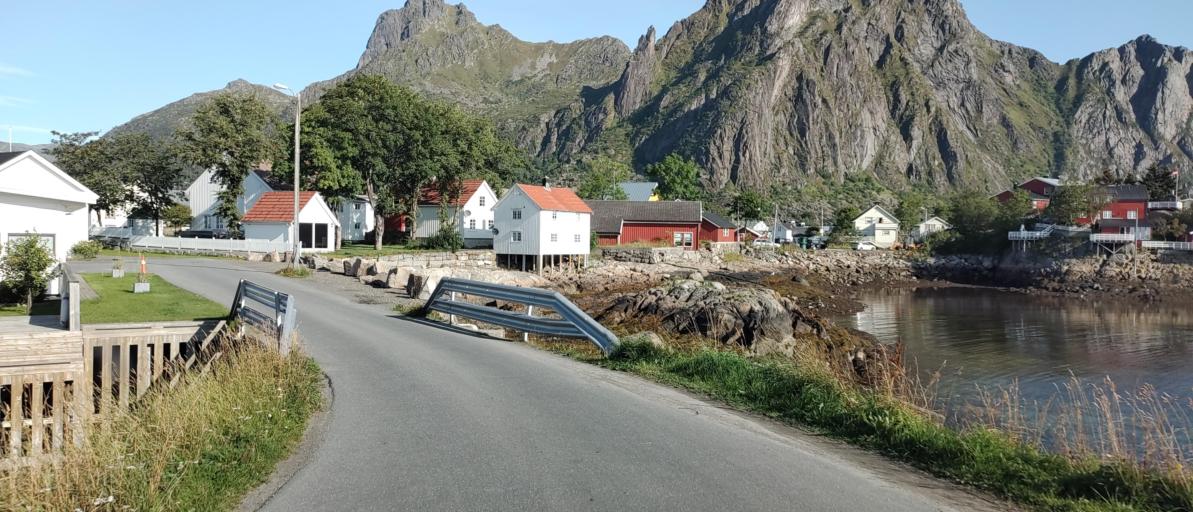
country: NO
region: Nordland
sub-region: Vagan
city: Svolvaer
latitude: 68.2333
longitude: 14.5806
